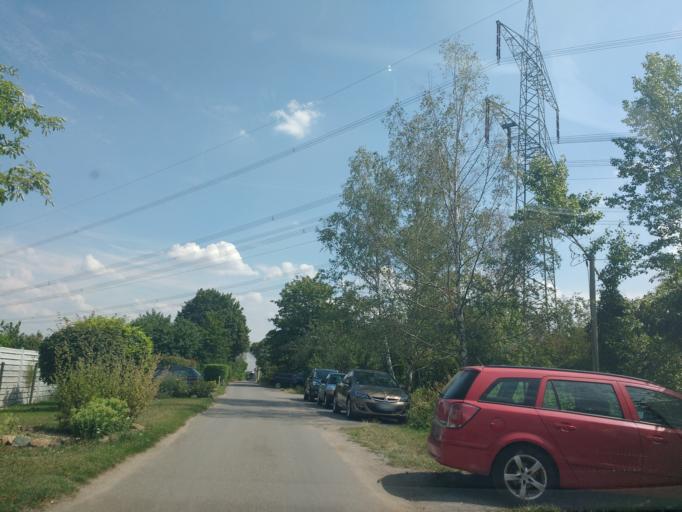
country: DE
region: Saxony-Anhalt
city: Dieskau
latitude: 51.4592
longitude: 12.0309
